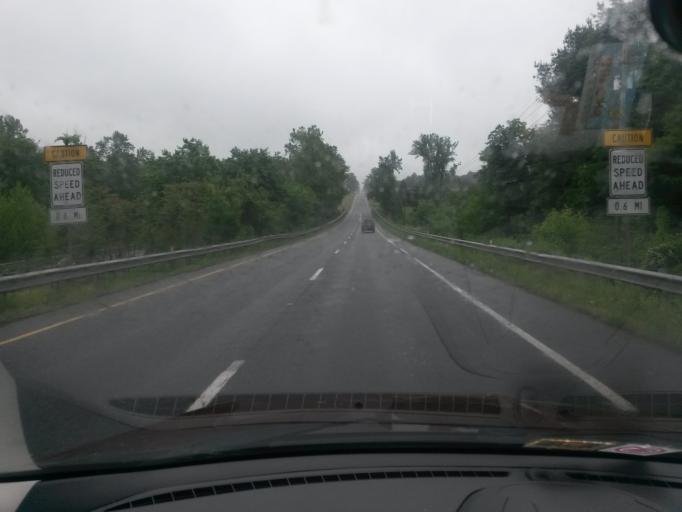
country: US
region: Virginia
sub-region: Greene County
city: Ruckersville
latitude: 38.2142
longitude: -78.3819
